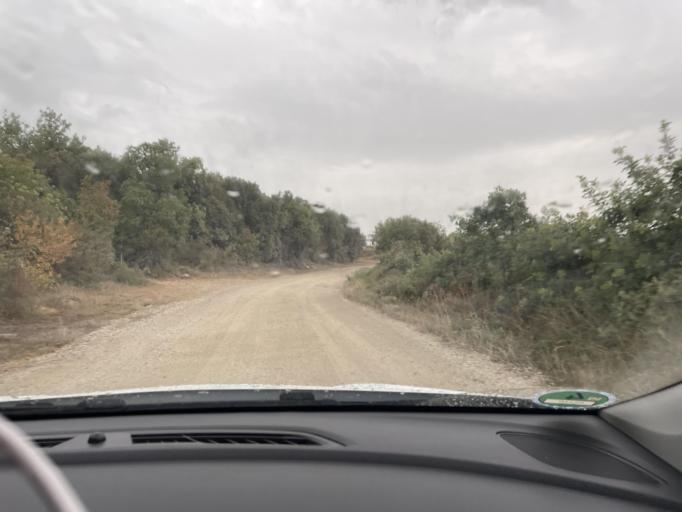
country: HR
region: Istarska
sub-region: Grad Rovinj
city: Rovinj
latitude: 45.0487
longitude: 13.7113
